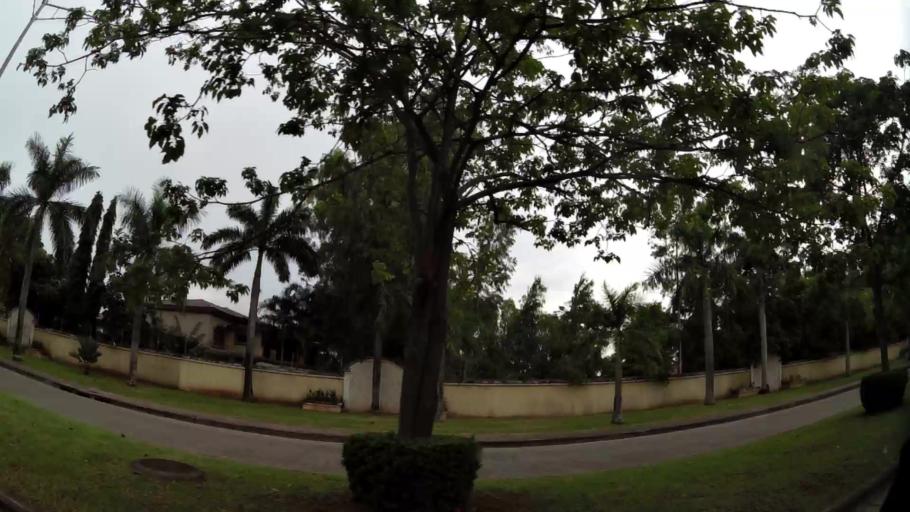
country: PA
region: Panama
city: San Miguelito
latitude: 9.0155
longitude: -79.4592
